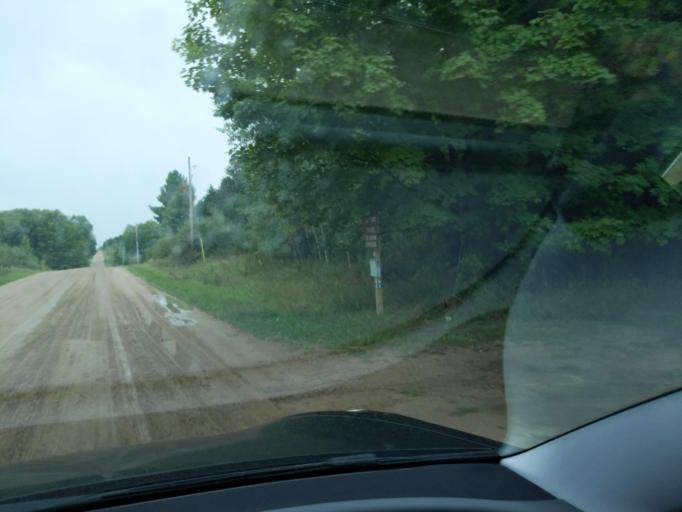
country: US
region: Michigan
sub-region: Antrim County
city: Elk Rapids
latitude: 44.8164
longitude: -85.3940
